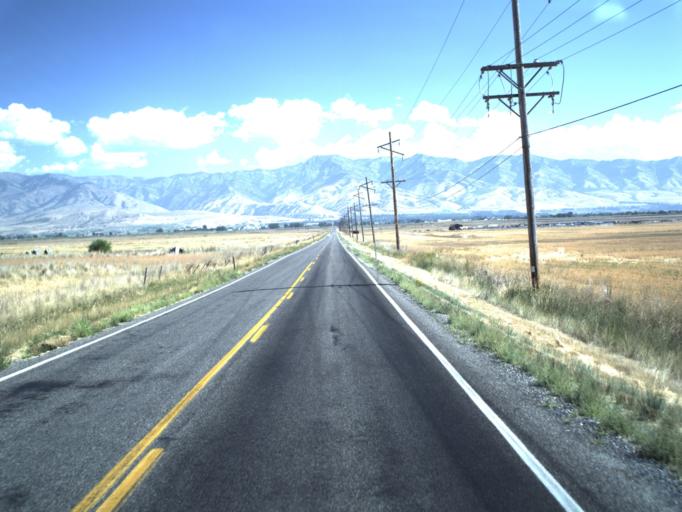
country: US
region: Utah
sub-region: Cache County
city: Benson
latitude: 41.8448
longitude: -111.9511
